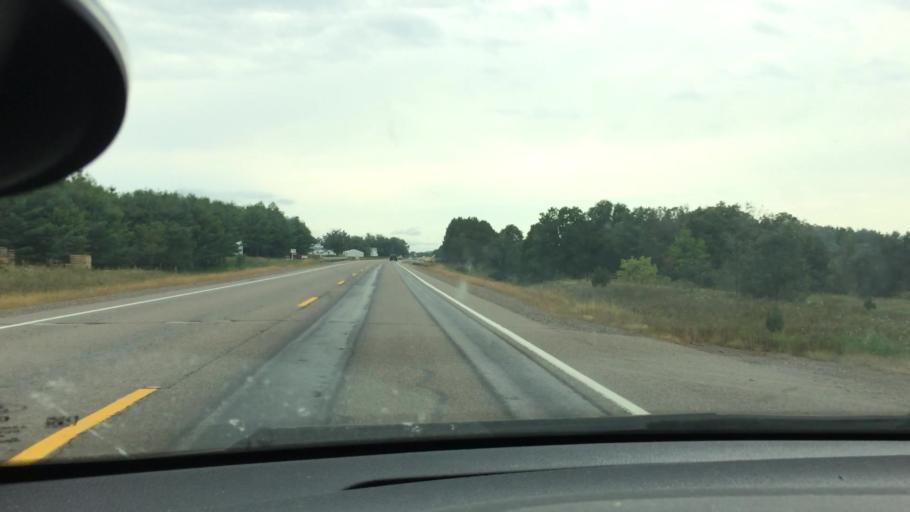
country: US
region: Wisconsin
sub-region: Eau Claire County
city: Augusta
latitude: 44.5846
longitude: -91.1107
